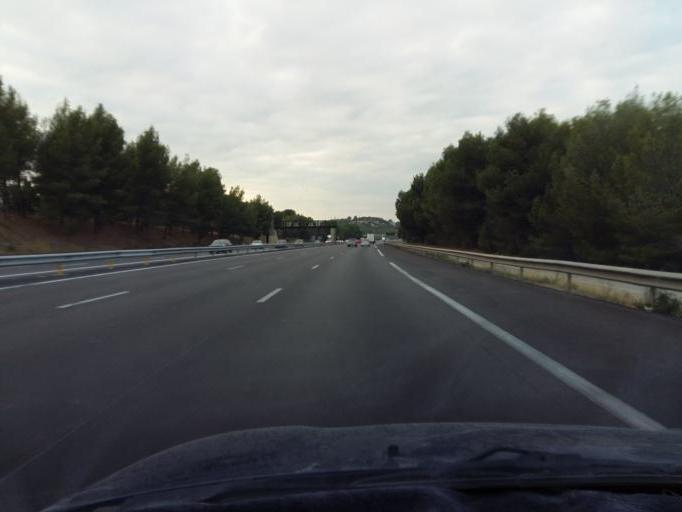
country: FR
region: Provence-Alpes-Cote d'Azur
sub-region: Departement des Bouches-du-Rhone
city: Lancon-Provence
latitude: 43.5961
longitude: 5.1662
